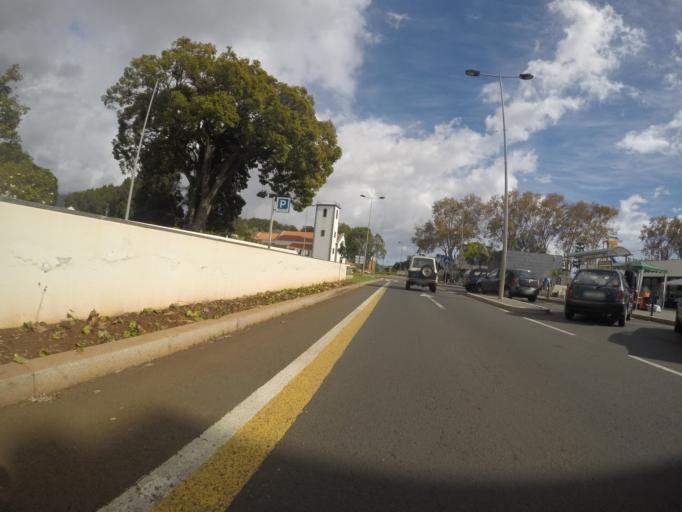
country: PT
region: Madeira
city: Camara de Lobos
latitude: 32.6501
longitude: -16.9435
